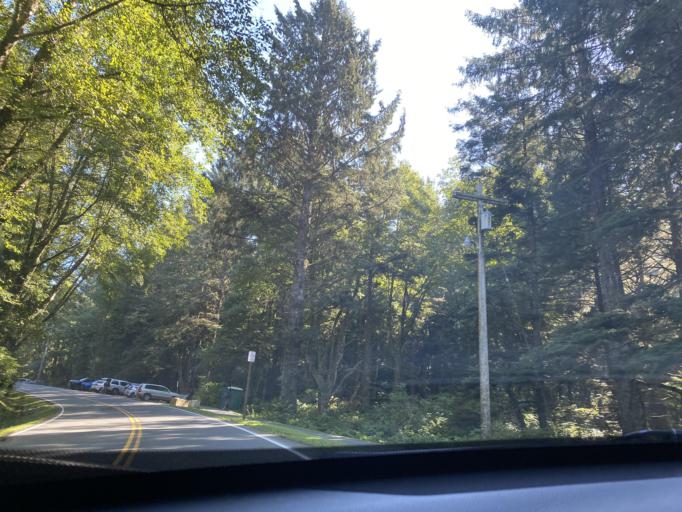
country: US
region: Washington
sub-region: Clallam County
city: Forks
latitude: 47.8984
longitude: -124.6249
